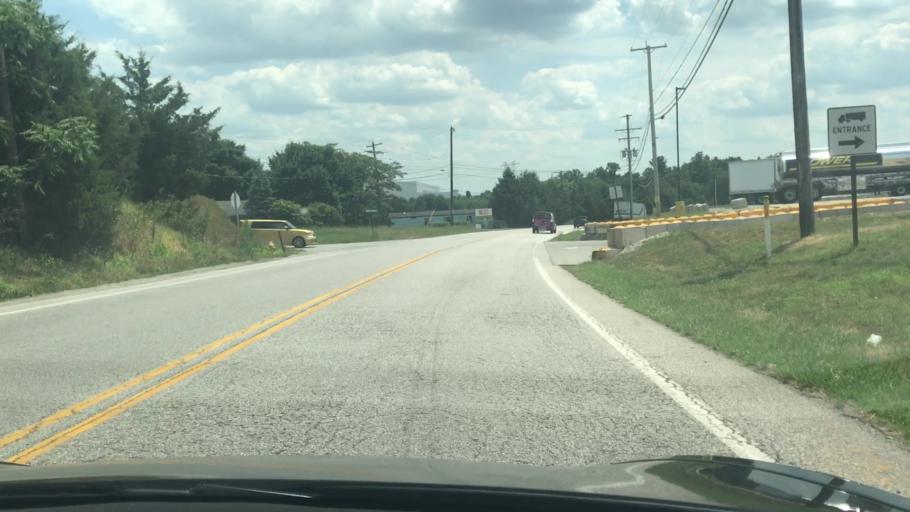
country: US
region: Pennsylvania
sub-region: York County
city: Manchester
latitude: 40.0779
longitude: -76.7655
